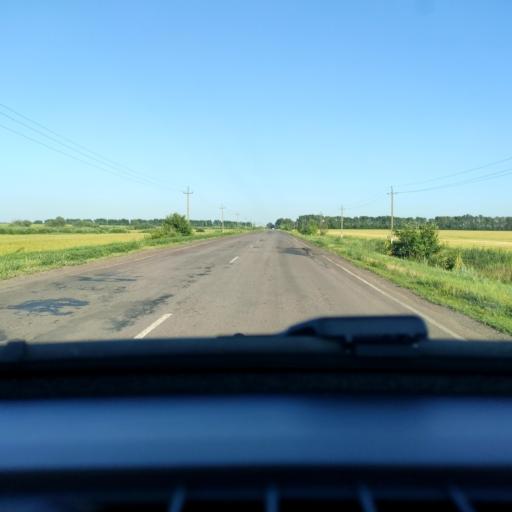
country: RU
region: Voronezj
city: Kashirskoye
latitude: 51.4951
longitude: 39.8389
